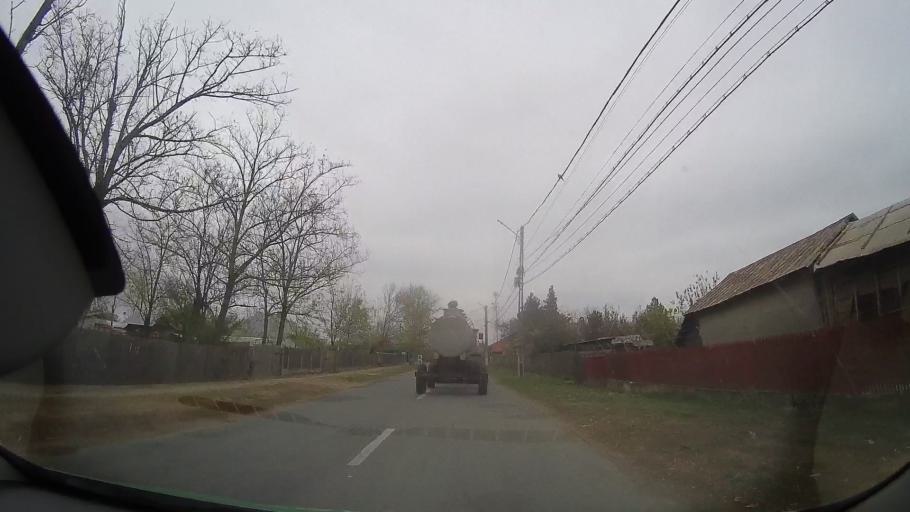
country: RO
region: Ialomita
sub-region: Comuna Grindu
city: Grindu
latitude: 44.7725
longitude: 26.9096
